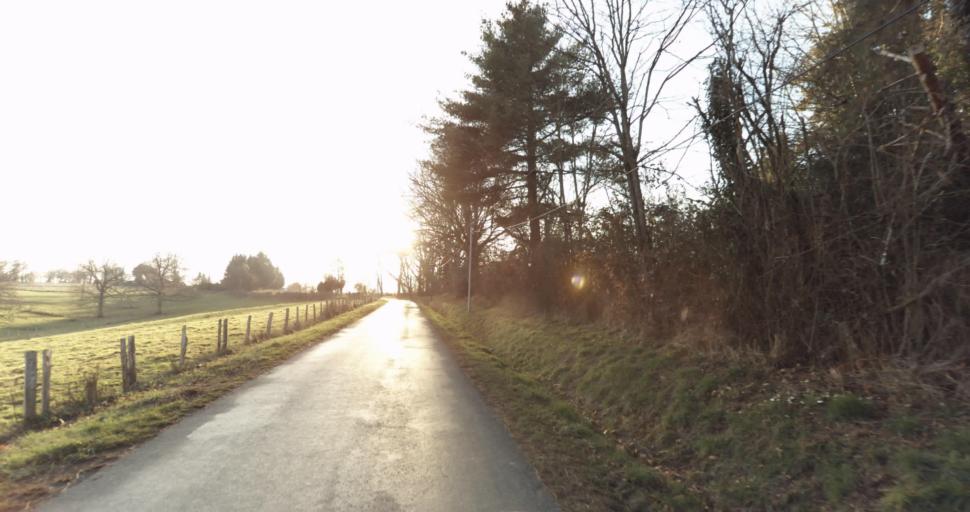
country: FR
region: Limousin
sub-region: Departement de la Haute-Vienne
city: Aixe-sur-Vienne
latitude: 45.7851
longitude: 1.1426
